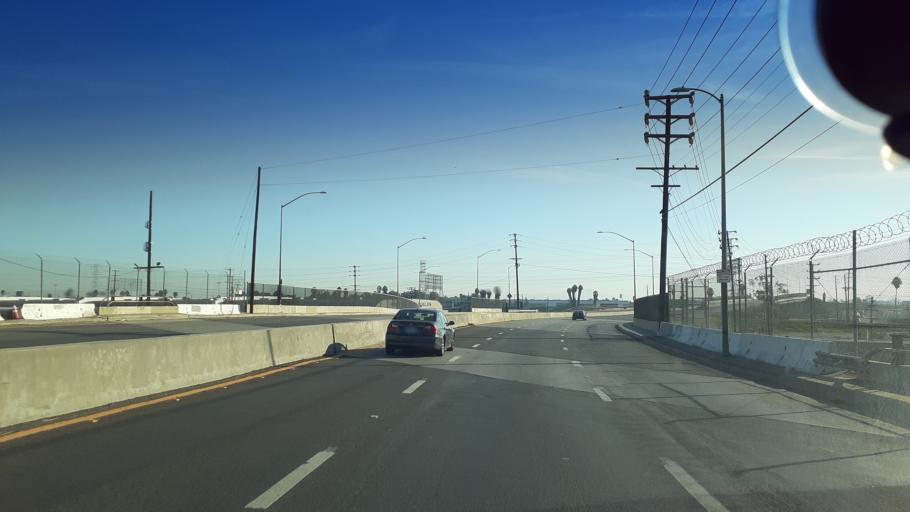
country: US
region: California
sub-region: Los Angeles County
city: Long Beach
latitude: 33.7916
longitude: -118.2325
